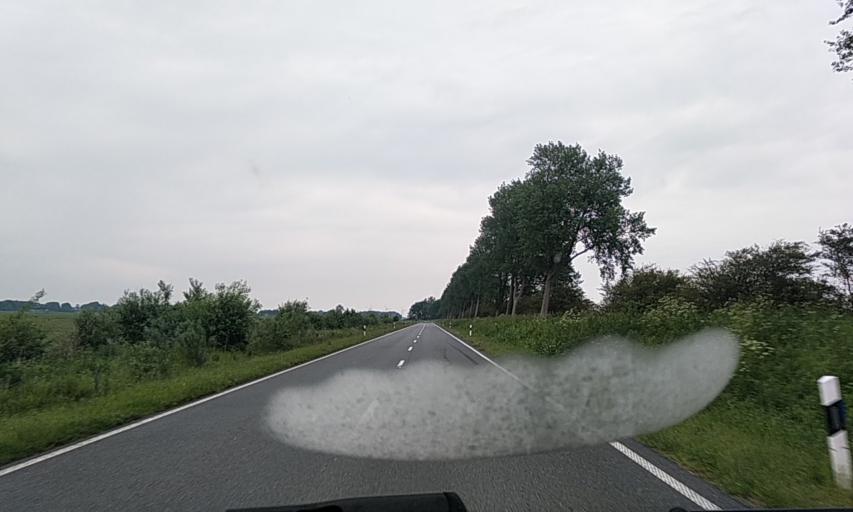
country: DE
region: Schleswig-Holstein
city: Meggerdorf
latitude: 54.3298
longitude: 9.3951
